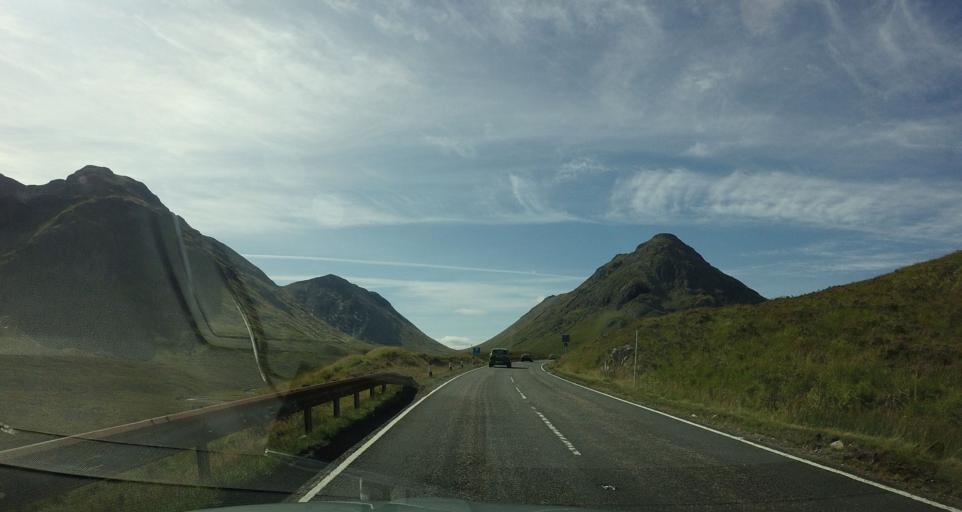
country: GB
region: Scotland
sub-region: Highland
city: Spean Bridge
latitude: 56.6624
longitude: -4.9098
